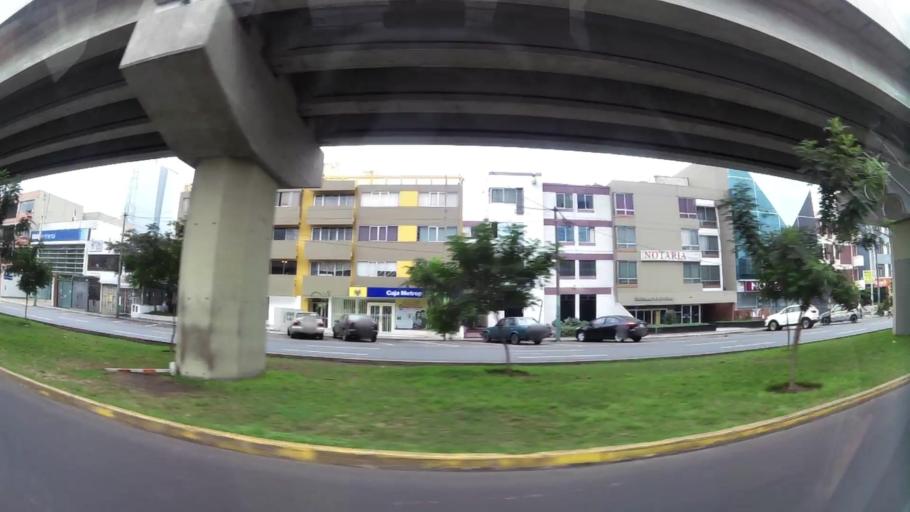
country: PE
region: Lima
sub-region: Lima
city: San Luis
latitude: -12.0903
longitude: -77.0033
